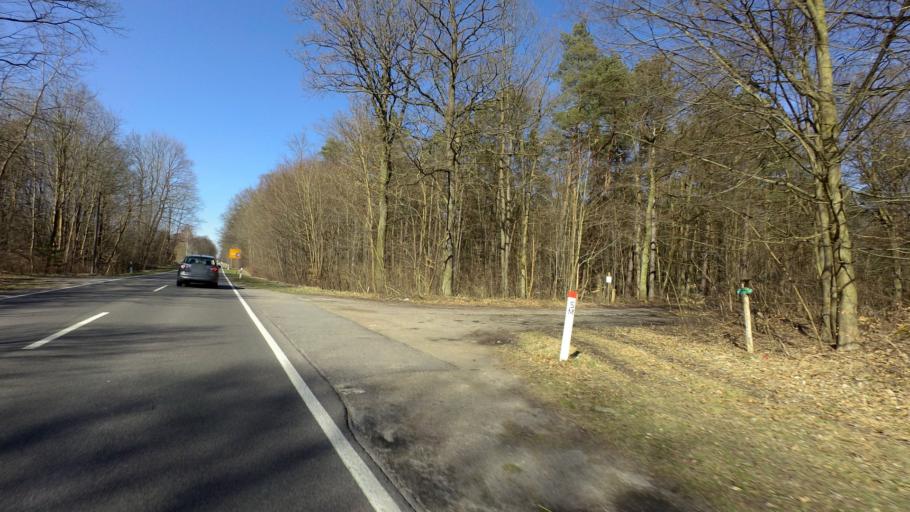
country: DE
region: Brandenburg
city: Eberswalde
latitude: 52.8183
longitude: 13.8325
